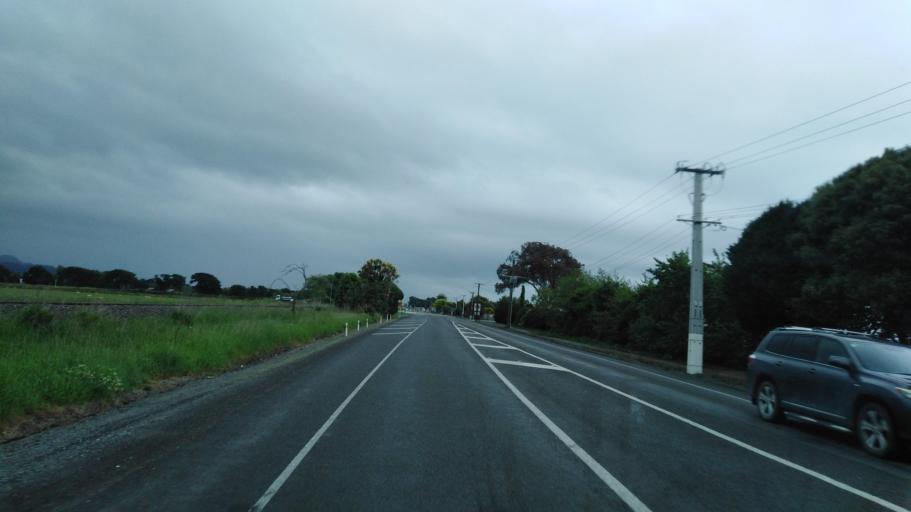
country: NZ
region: Manawatu-Wanganui
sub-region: Horowhenua District
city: Levin
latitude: -40.6461
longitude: 175.2625
